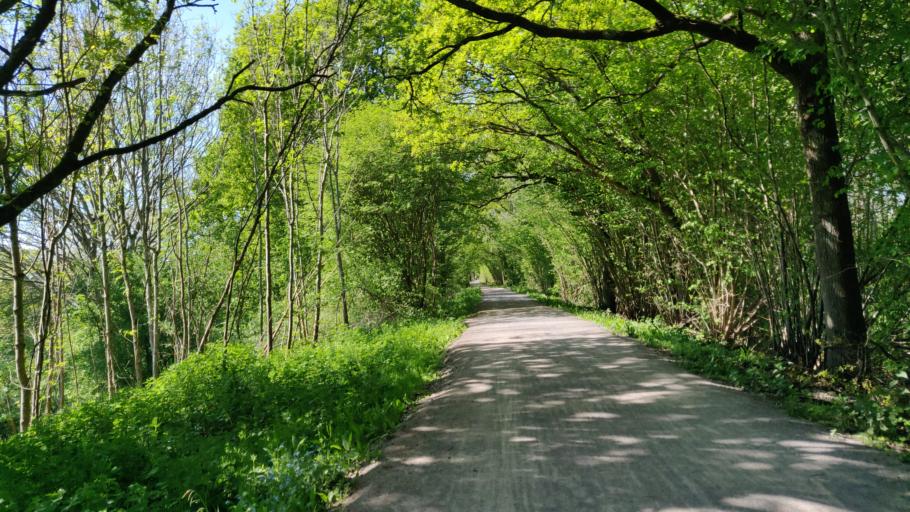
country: GB
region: England
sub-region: West Sussex
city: Rudgwick
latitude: 51.0824
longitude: -0.4375
